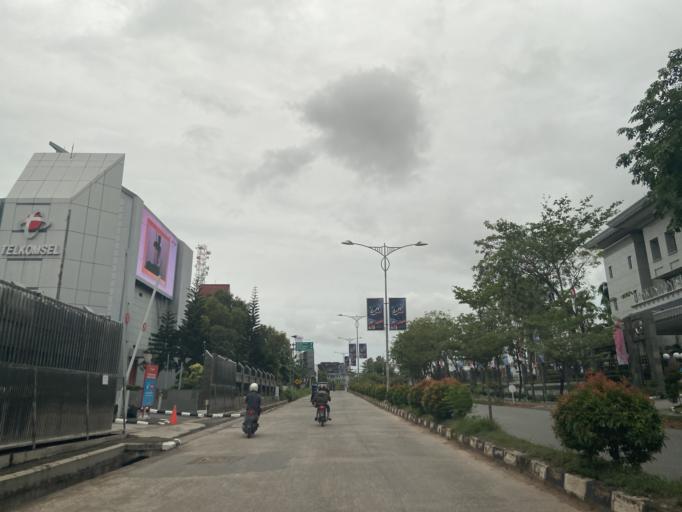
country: SG
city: Singapore
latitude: 1.1288
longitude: 104.0571
